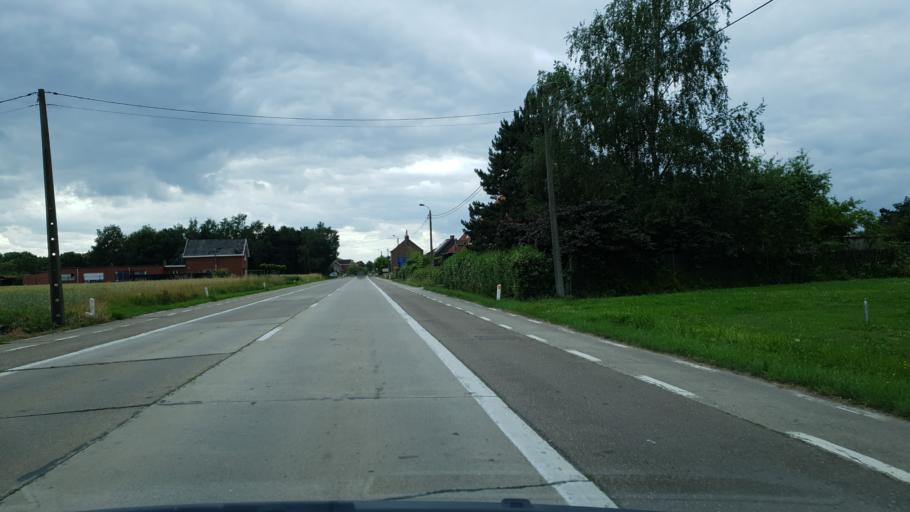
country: BE
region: Flanders
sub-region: Provincie Antwerpen
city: Hulshout
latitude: 51.0580
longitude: 4.8086
